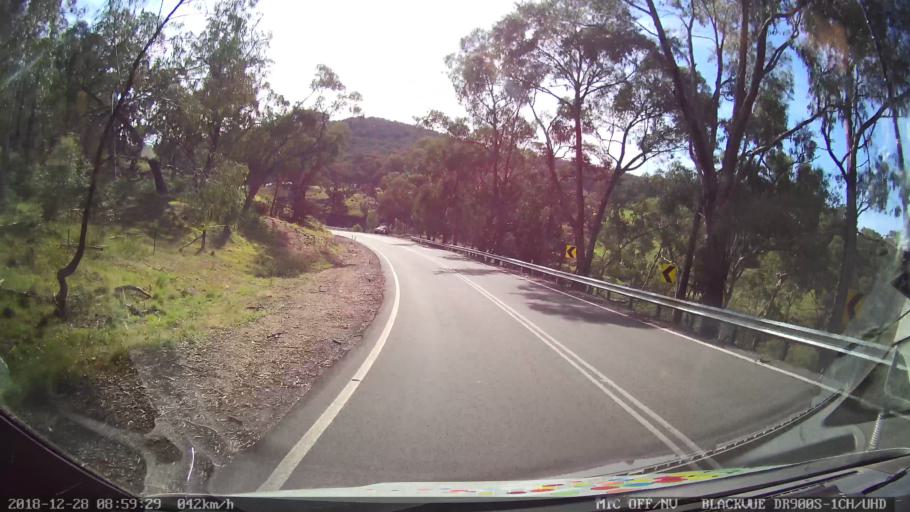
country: AU
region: New South Wales
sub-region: Upper Lachlan Shire
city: Crookwell
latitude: -34.1342
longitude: 149.3318
